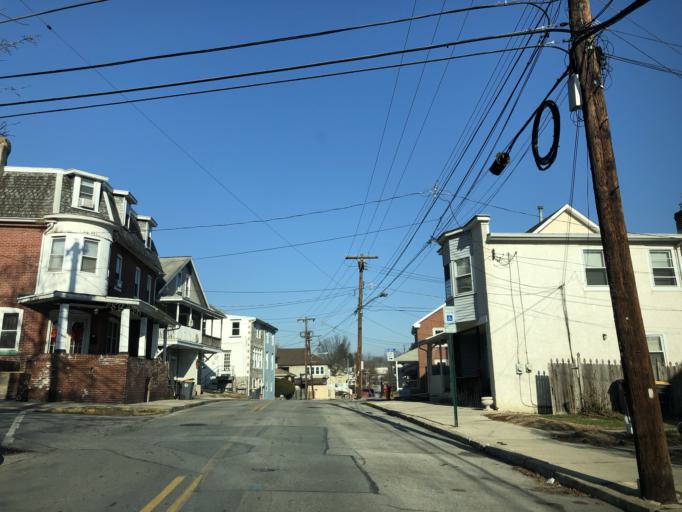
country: US
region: Pennsylvania
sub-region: Chester County
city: Downingtown
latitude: 39.9986
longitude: -75.7101
